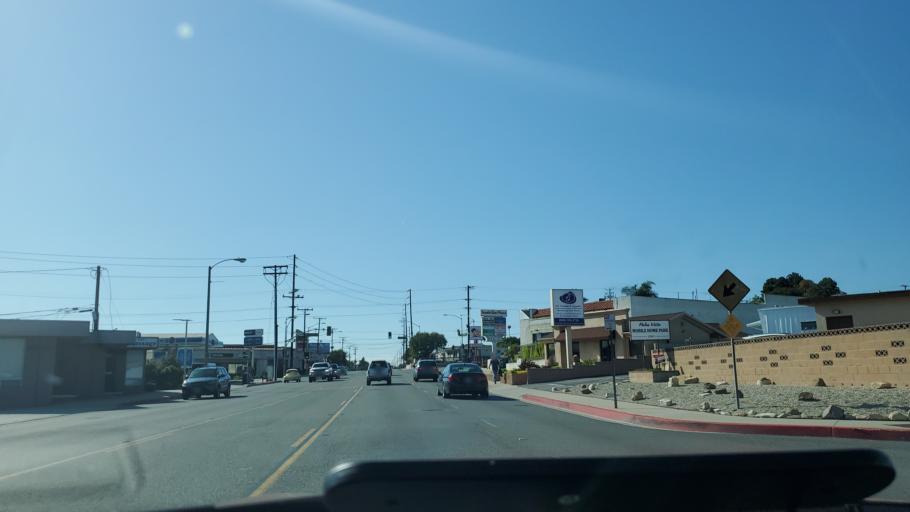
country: US
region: California
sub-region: Los Angeles County
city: Lomita
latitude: 33.8043
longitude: -118.3242
